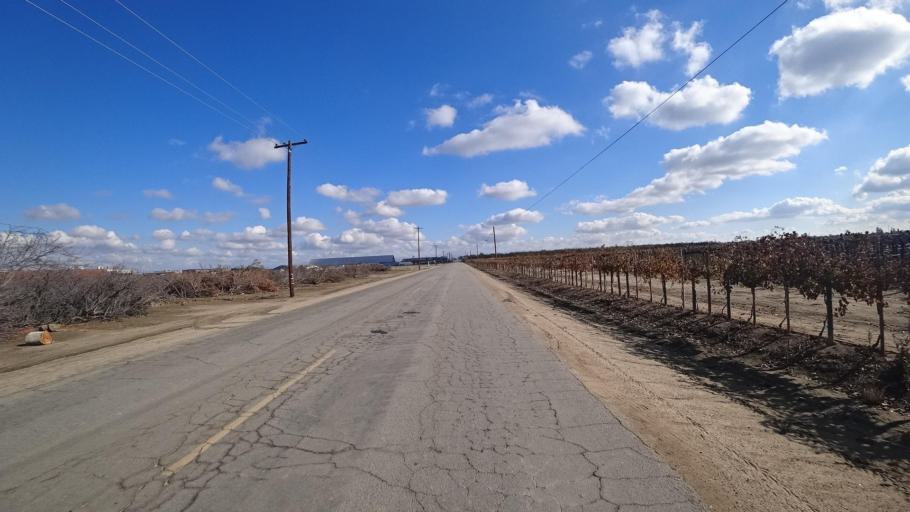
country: US
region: California
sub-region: Kern County
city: McFarland
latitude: 35.6888
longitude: -119.2469
